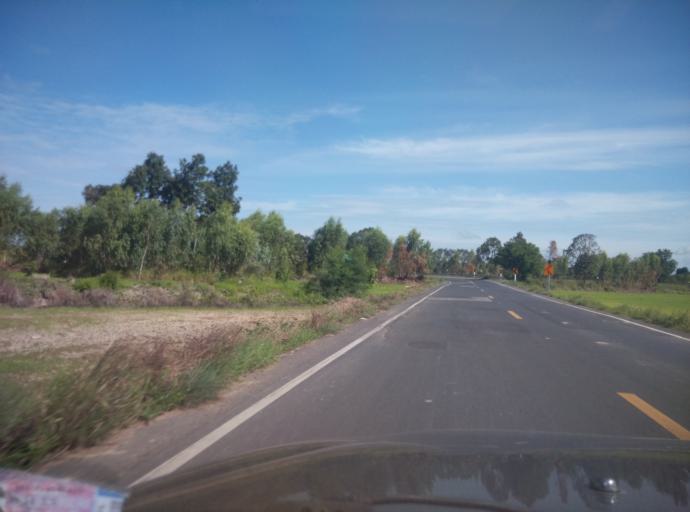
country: TH
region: Sisaket
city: Si Sa Ket
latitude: 15.1225
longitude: 104.2498
